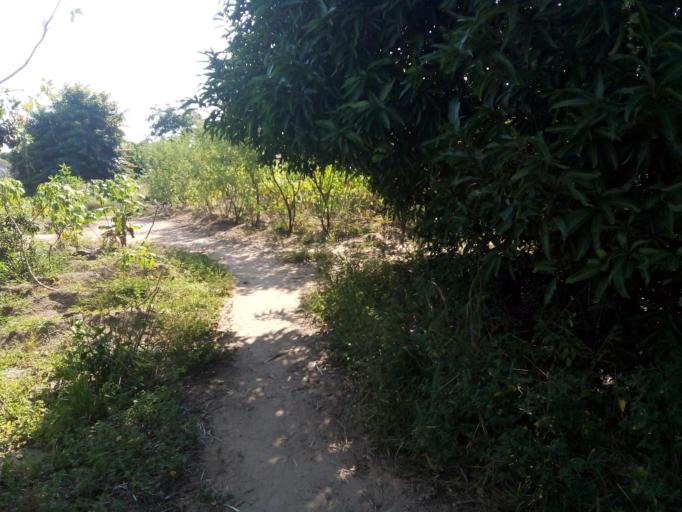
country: MZ
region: Zambezia
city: Quelimane
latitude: -17.5546
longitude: 36.7017
